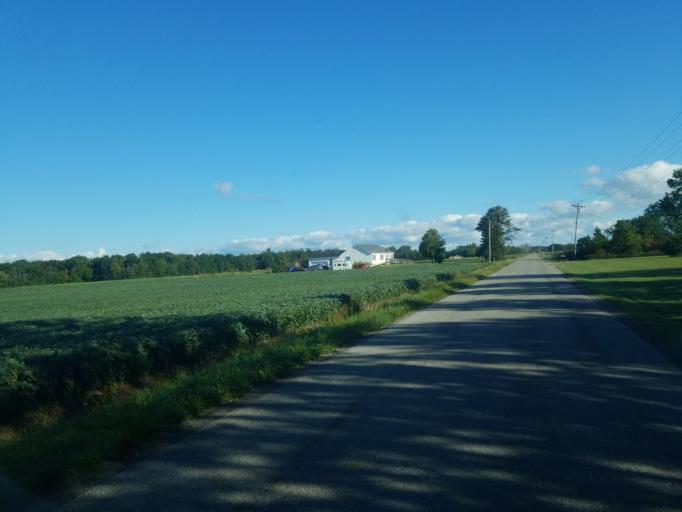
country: US
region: Ohio
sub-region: Lorain County
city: Camden
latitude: 41.2266
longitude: -82.3210
